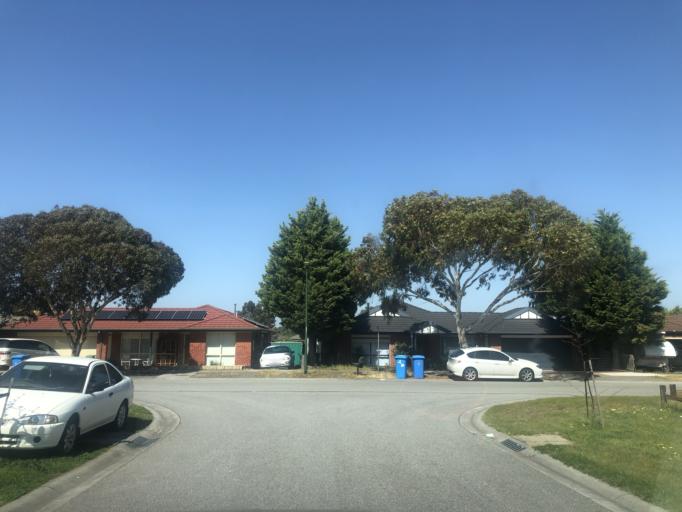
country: AU
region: Victoria
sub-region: Casey
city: Lynbrook
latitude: -38.0486
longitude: 145.2687
